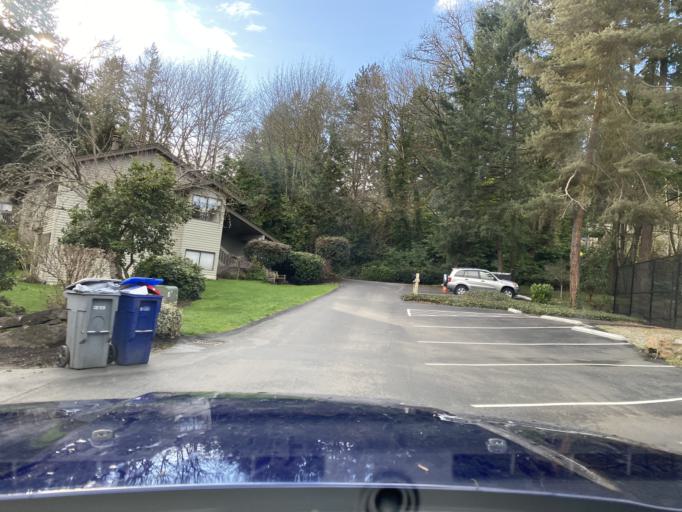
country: US
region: Washington
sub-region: King County
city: Bellevue
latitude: 47.5988
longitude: -122.1932
